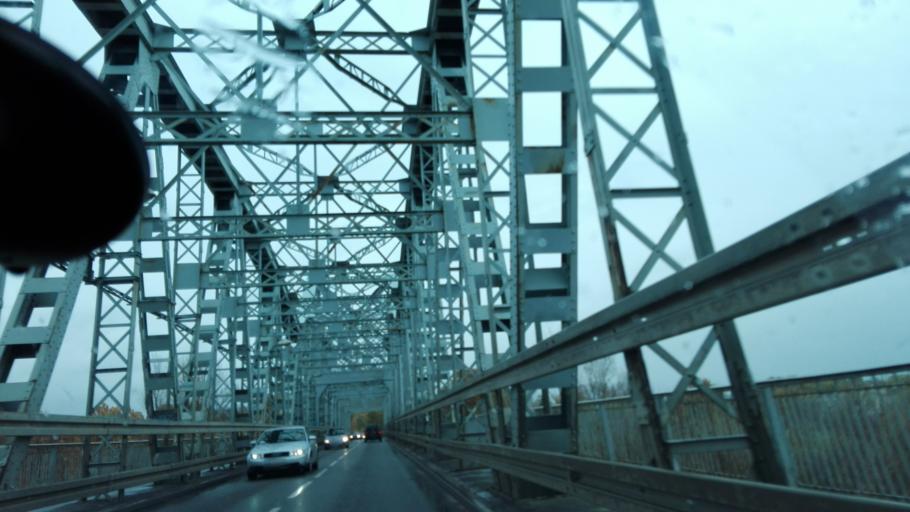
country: PL
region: Lublin Voivodeship
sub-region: Powiat pulawski
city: Pulawy
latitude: 51.4135
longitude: 21.9467
